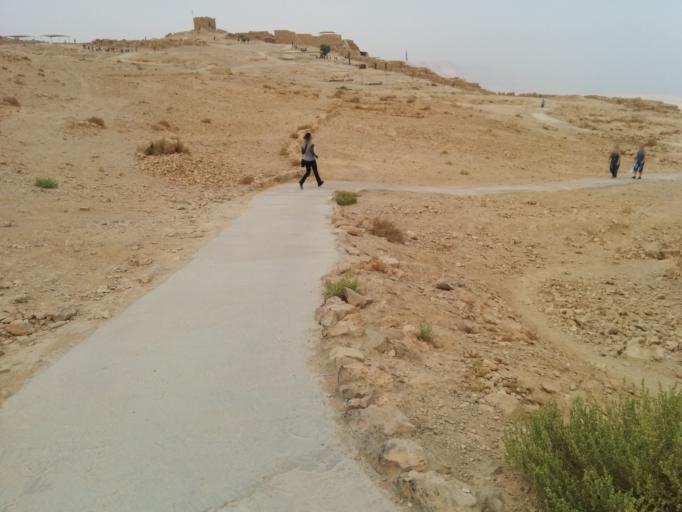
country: IL
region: Southern District
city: `En Boqeq
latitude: 31.3145
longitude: 35.3547
